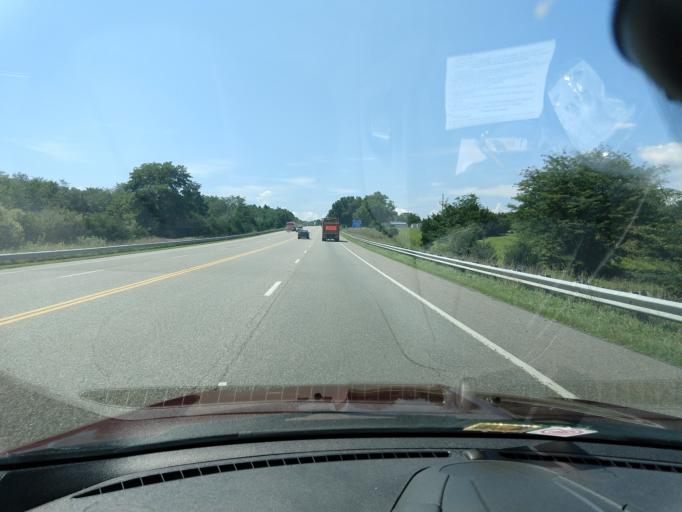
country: US
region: Virginia
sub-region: City of Harrisonburg
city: Harrisonburg
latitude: 38.4973
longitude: -78.8703
